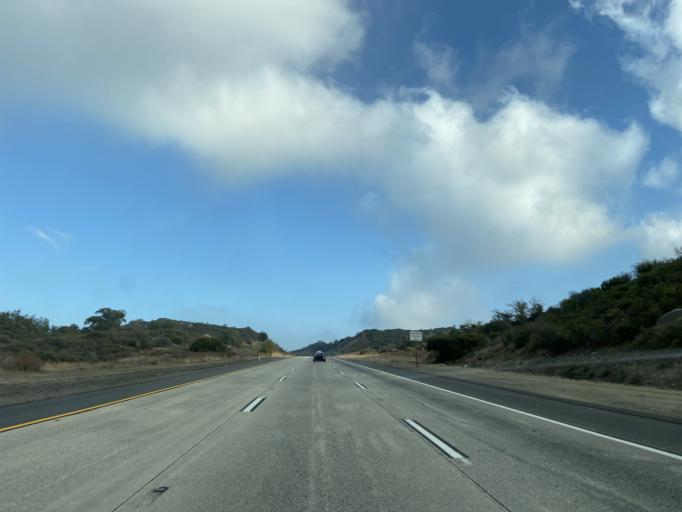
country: US
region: California
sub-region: San Diego County
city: Descanso
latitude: 32.8200
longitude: -116.5891
